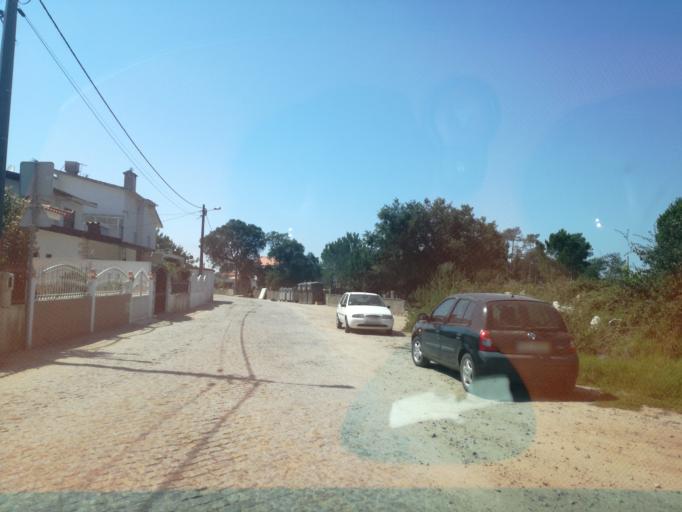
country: PT
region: Braga
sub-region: Esposende
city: Apulia
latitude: 41.4552
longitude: -8.7441
